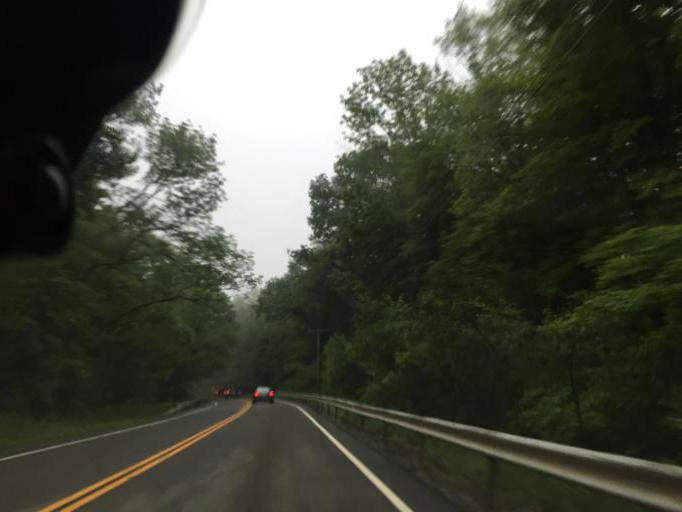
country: US
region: Connecticut
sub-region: Litchfield County
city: Winchester Center
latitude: 41.8871
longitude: -73.2553
